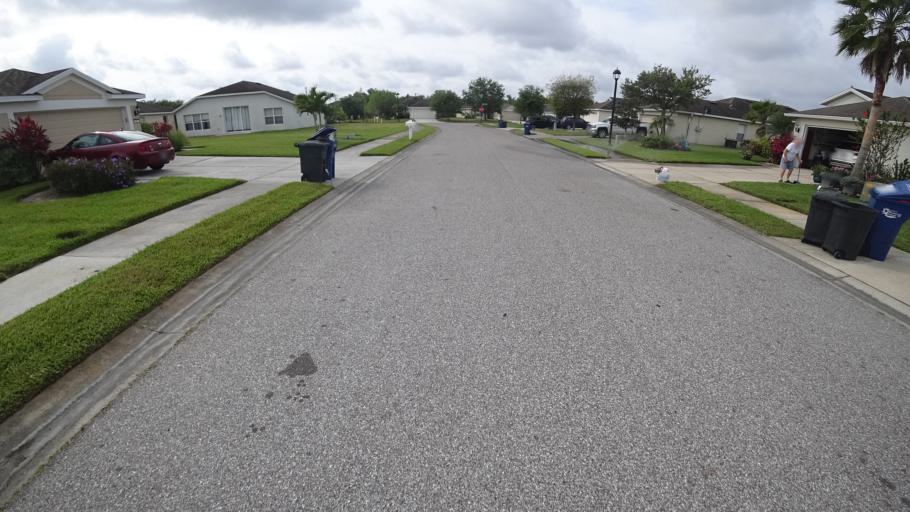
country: US
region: Florida
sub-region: Manatee County
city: Ellenton
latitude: 27.5589
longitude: -82.4627
